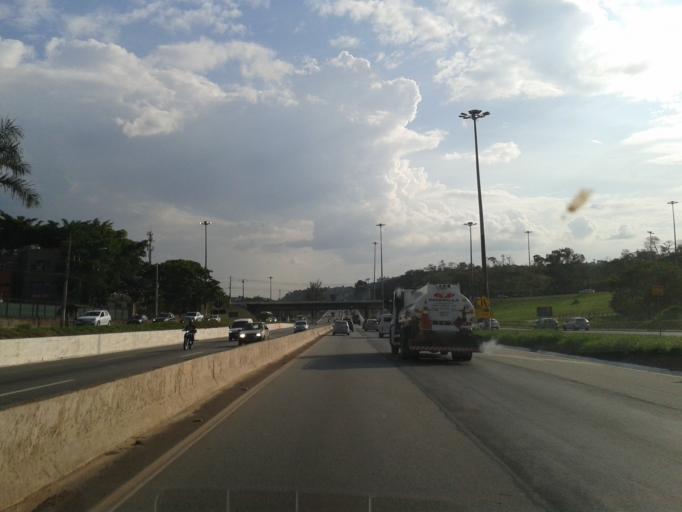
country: BR
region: Minas Gerais
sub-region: Belo Horizonte
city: Belo Horizonte
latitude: -19.8856
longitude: -43.9673
